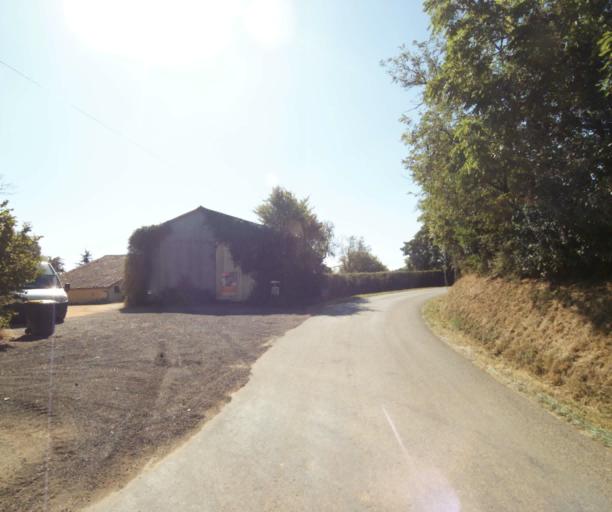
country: FR
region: Midi-Pyrenees
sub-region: Departement du Tarn-et-Garonne
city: Verdun-sur-Garonne
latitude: 43.8418
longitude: 1.2020
